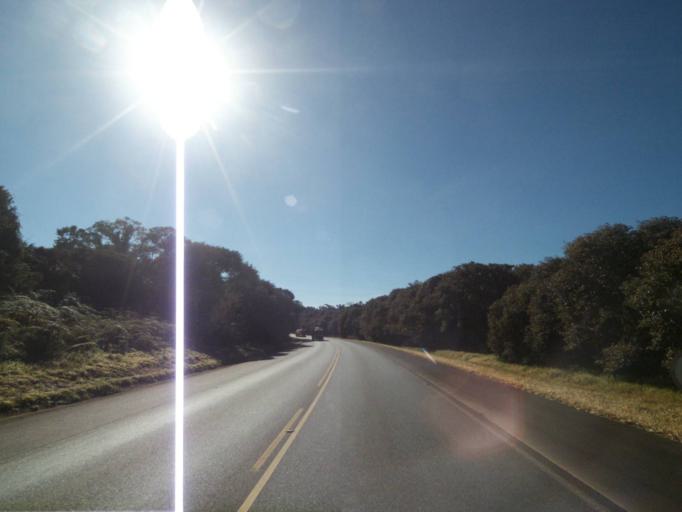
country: BR
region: Parana
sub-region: Tibagi
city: Tibagi
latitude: -24.4269
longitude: -50.3991
